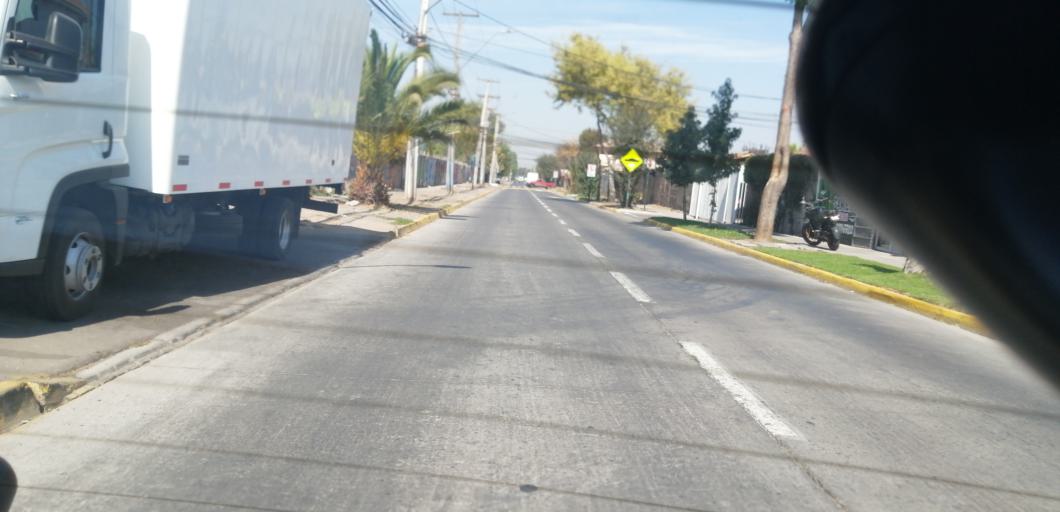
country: CL
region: Santiago Metropolitan
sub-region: Provincia de Santiago
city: Lo Prado
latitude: -33.4542
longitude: -70.7444
